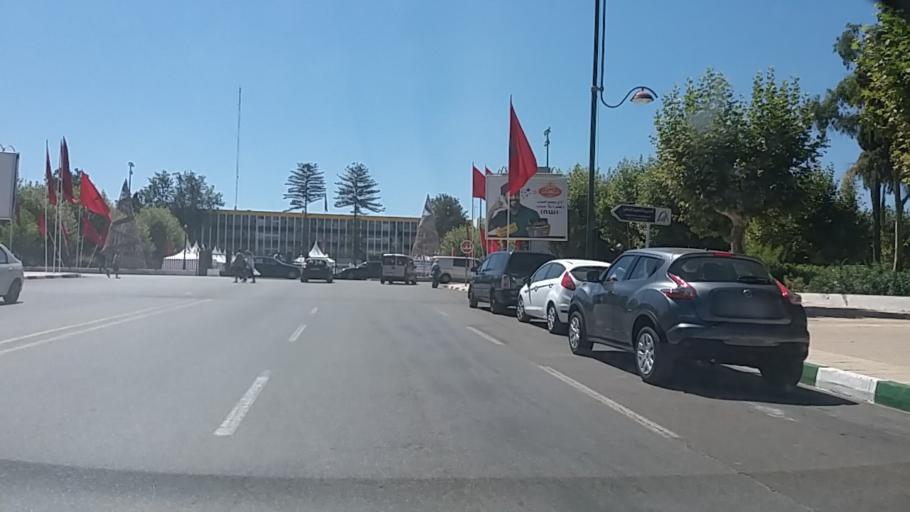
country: MA
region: Gharb-Chrarda-Beni Hssen
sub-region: Kenitra Province
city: Kenitra
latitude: 34.2572
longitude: -6.5796
